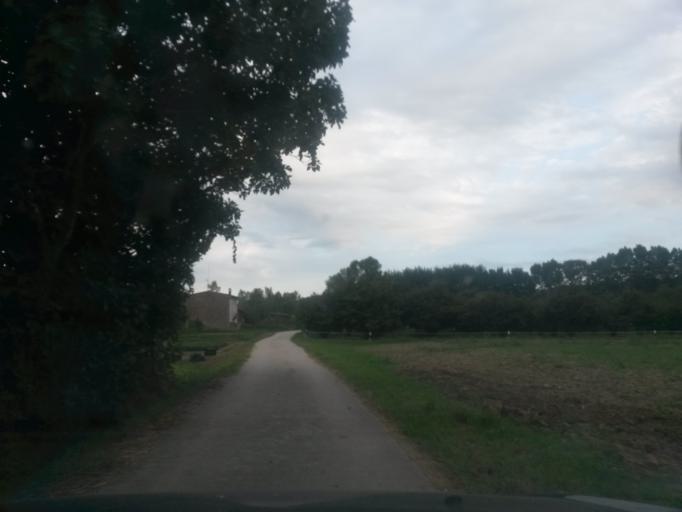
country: ES
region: Catalonia
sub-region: Provincia de Girona
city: Sant Gregori
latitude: 41.9731
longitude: 2.7164
